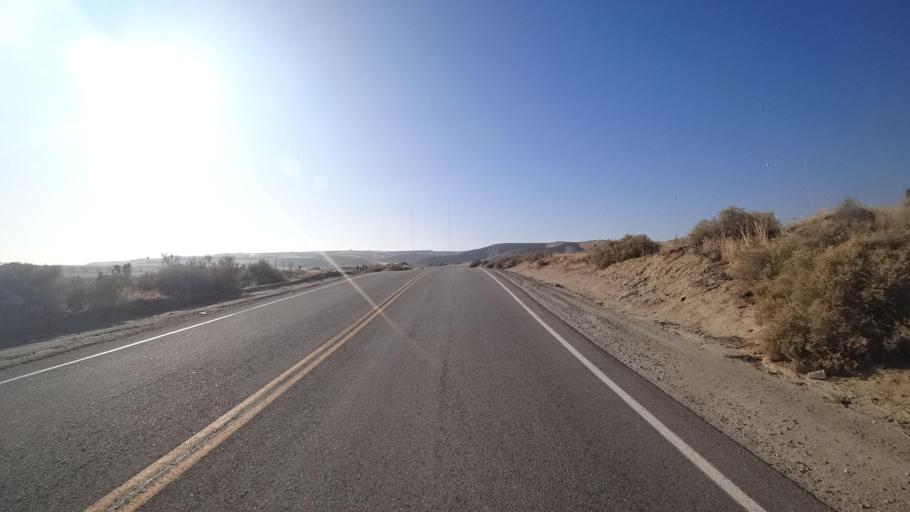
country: US
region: California
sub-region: Kern County
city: Oildale
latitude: 35.4509
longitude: -118.9421
